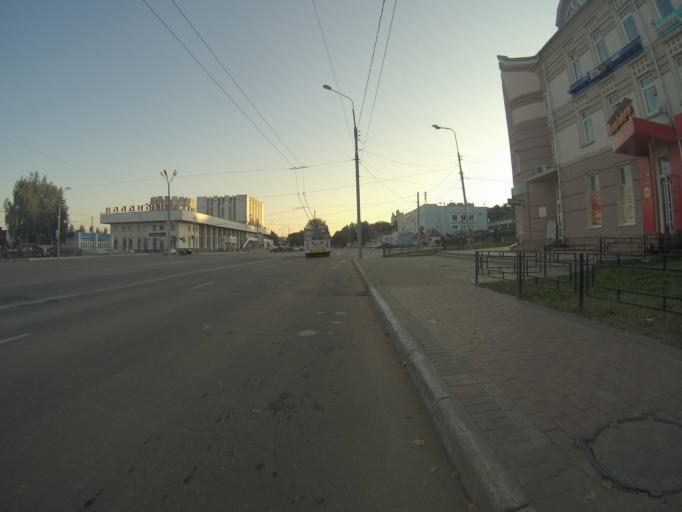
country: RU
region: Vladimir
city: Vladimir
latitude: 56.1313
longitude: 40.4214
